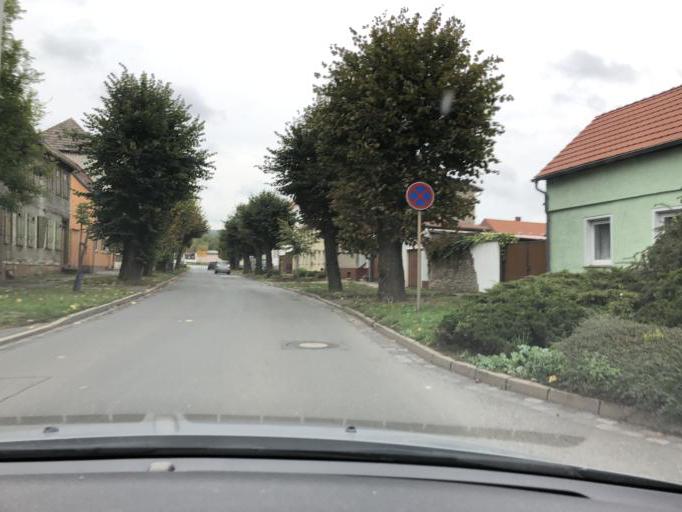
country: DE
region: Saxony-Anhalt
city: Rossla
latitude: 51.4613
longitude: 11.0740
